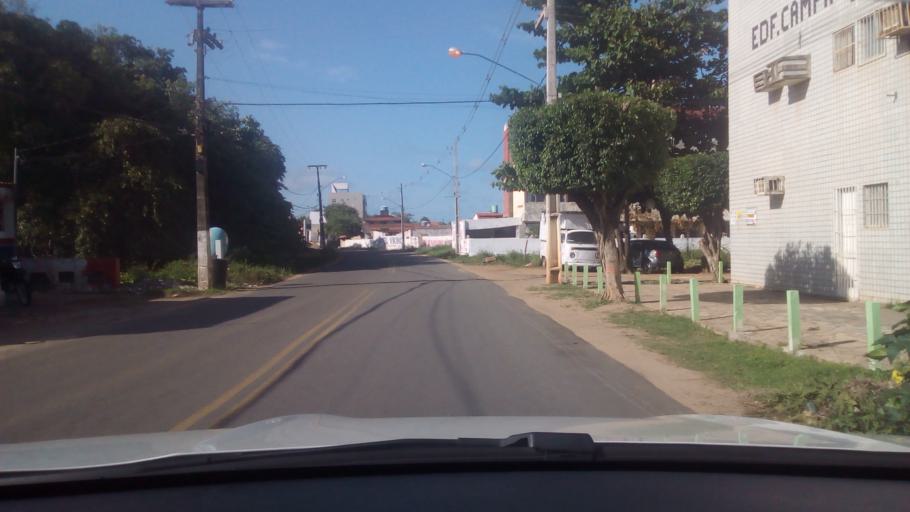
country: BR
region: Paraiba
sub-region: Conde
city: Conde
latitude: -7.2799
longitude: -34.8008
